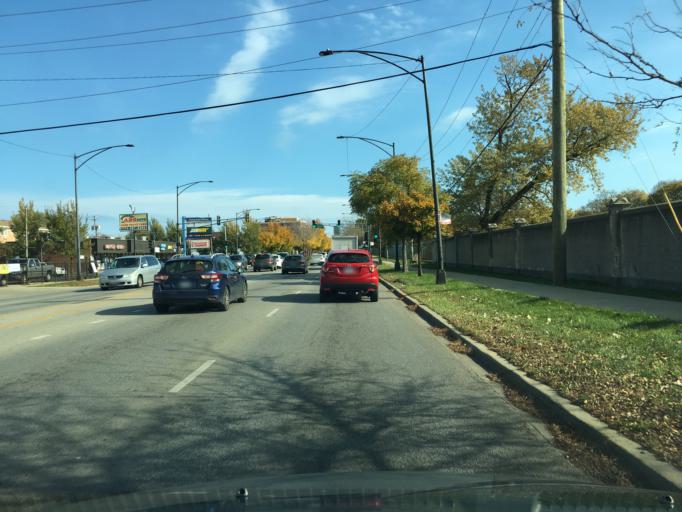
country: US
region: Illinois
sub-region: Cook County
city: Lincolnwood
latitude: 41.9906
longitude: -87.6809
